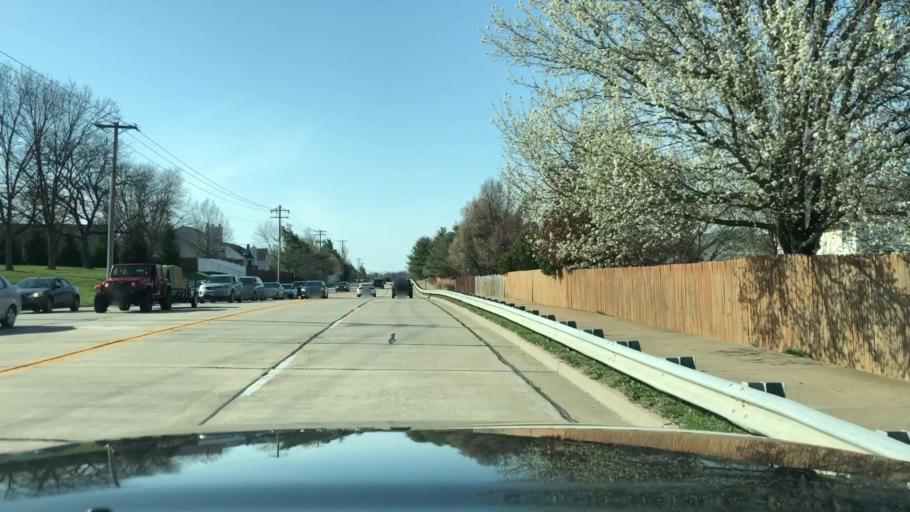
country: US
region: Missouri
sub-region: Saint Charles County
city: Saint Charles
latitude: 38.7729
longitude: -90.5501
